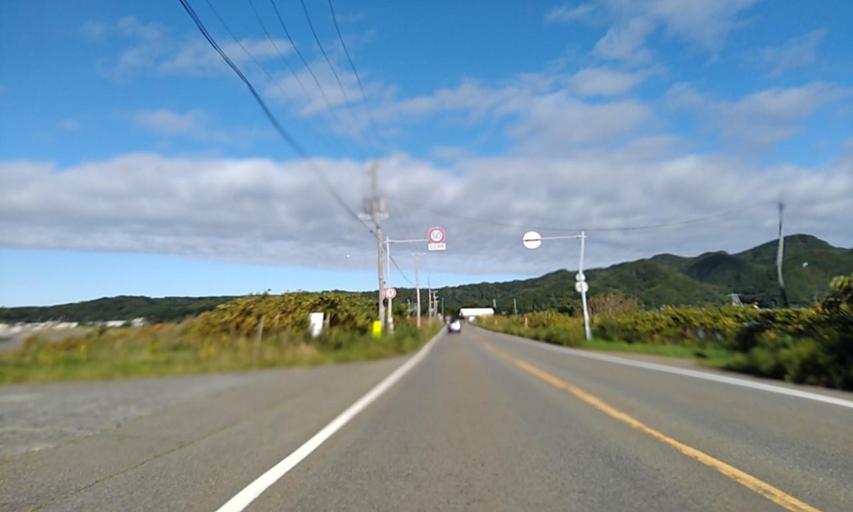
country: JP
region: Hokkaido
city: Shizunai-furukawacho
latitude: 42.2671
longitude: 142.5115
